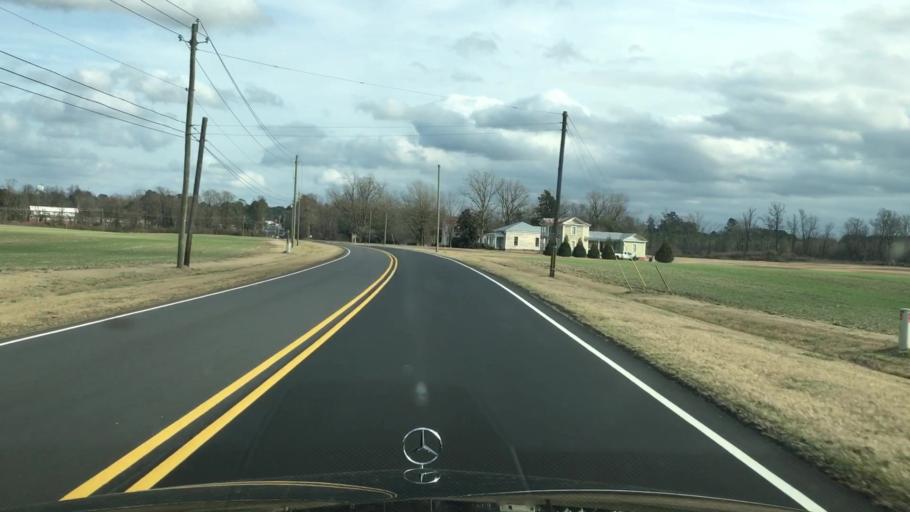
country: US
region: North Carolina
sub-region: Duplin County
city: Kenansville
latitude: 34.9588
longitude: -77.9834
